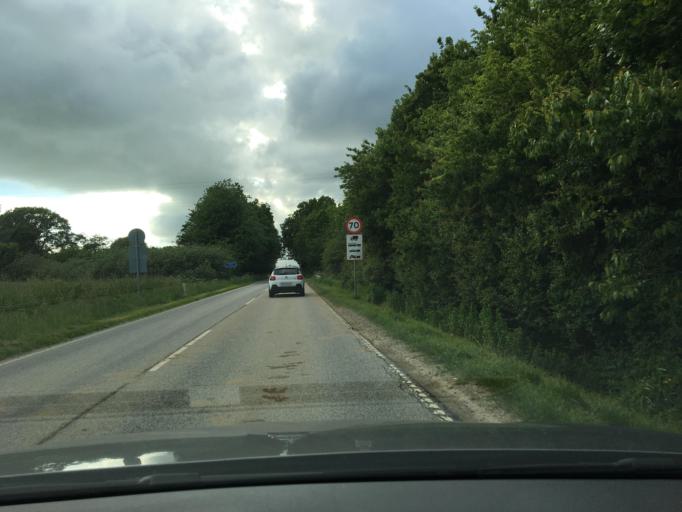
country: DK
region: Central Jutland
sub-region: Arhus Kommune
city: Logten
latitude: 56.2908
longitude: 10.2977
